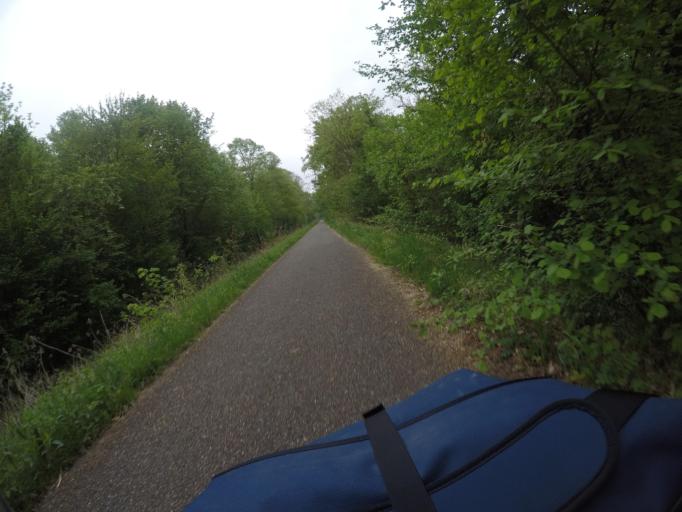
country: FR
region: Alsace
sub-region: Departement du Bas-Rhin
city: La Wantzenau
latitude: 48.6278
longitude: 7.8219
